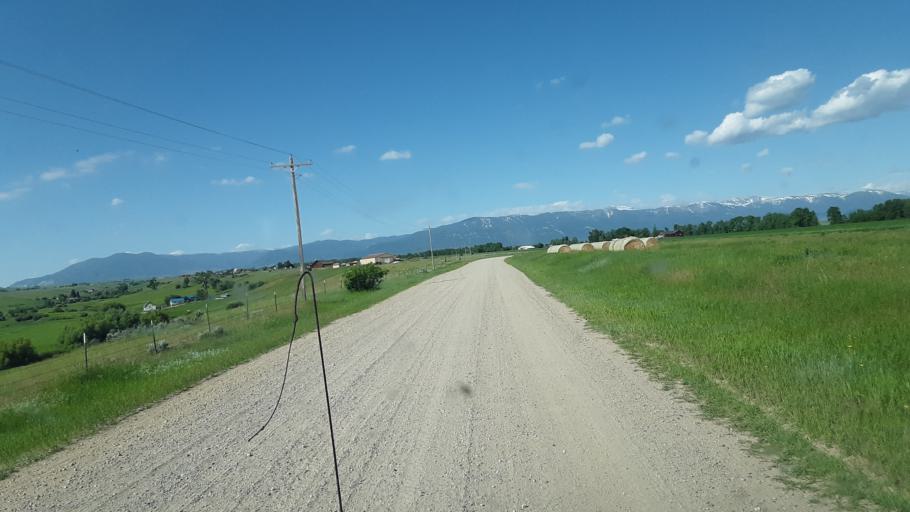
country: US
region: Montana
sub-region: Carbon County
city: Red Lodge
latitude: 45.3295
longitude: -109.1678
